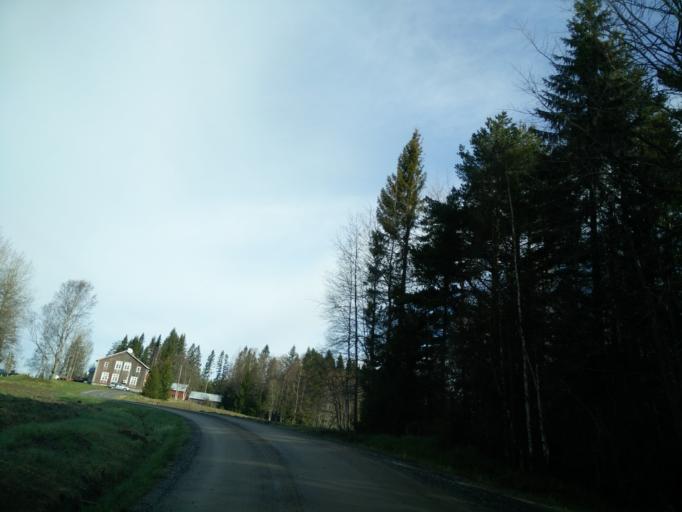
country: SE
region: Vaesternorrland
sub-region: Haernoesands Kommun
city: Haernoesand
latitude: 62.6035
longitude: 17.7398
